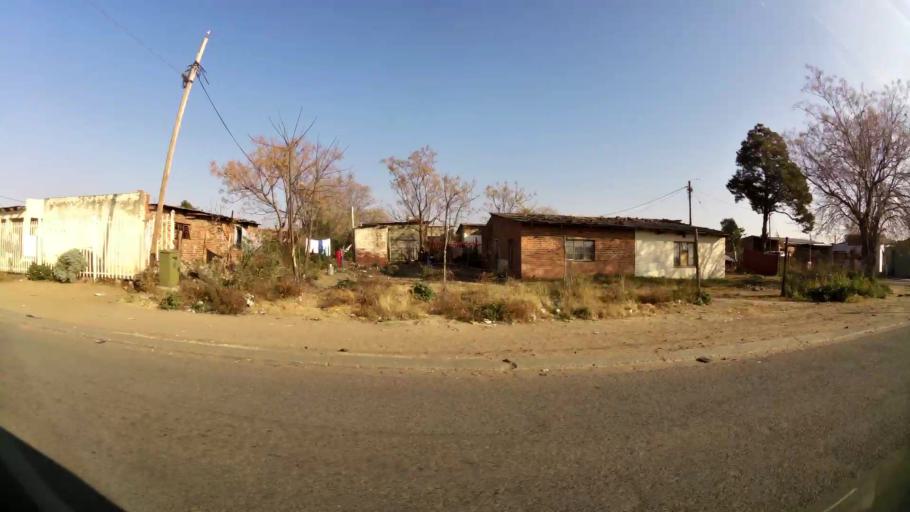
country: ZA
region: Orange Free State
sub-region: Mangaung Metropolitan Municipality
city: Bloemfontein
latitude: -29.1386
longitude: 26.2515
